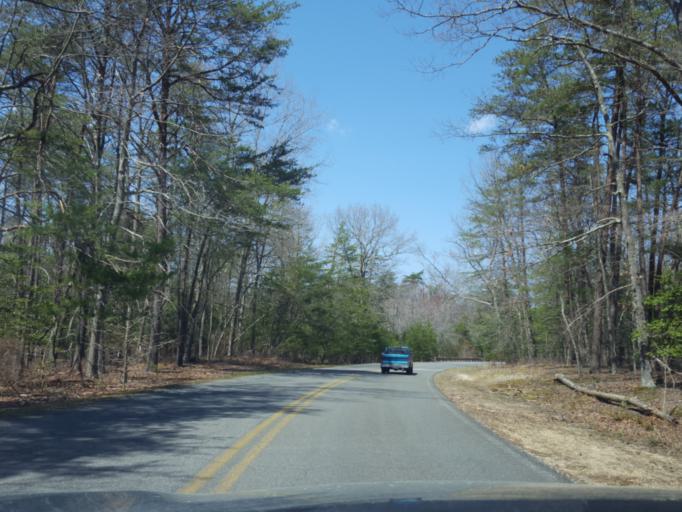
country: US
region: Maryland
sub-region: Prince George's County
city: Brandywine
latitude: 38.6532
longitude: -76.8332
